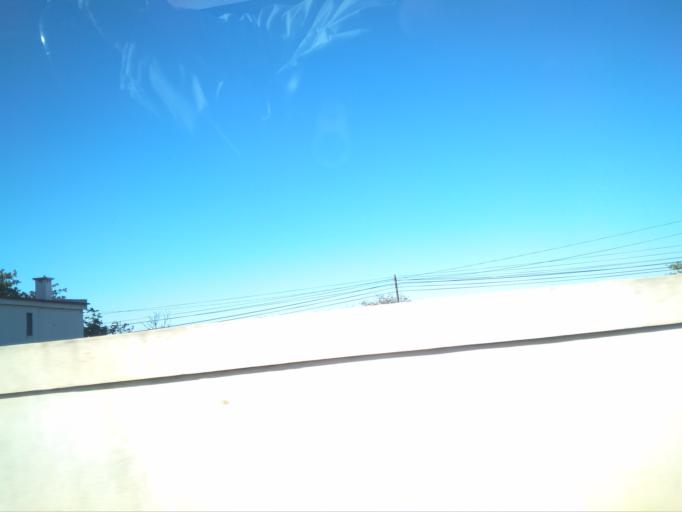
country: PT
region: Faro
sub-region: Faro
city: Santa Barbara de Nexe
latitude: 37.0966
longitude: -7.9637
